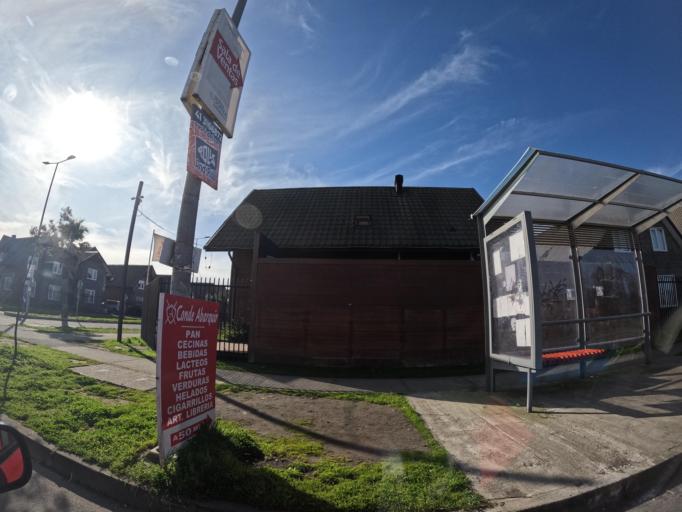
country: CL
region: Biobio
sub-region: Provincia de Concepcion
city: Concepcion
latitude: -36.7702
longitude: -73.0703
